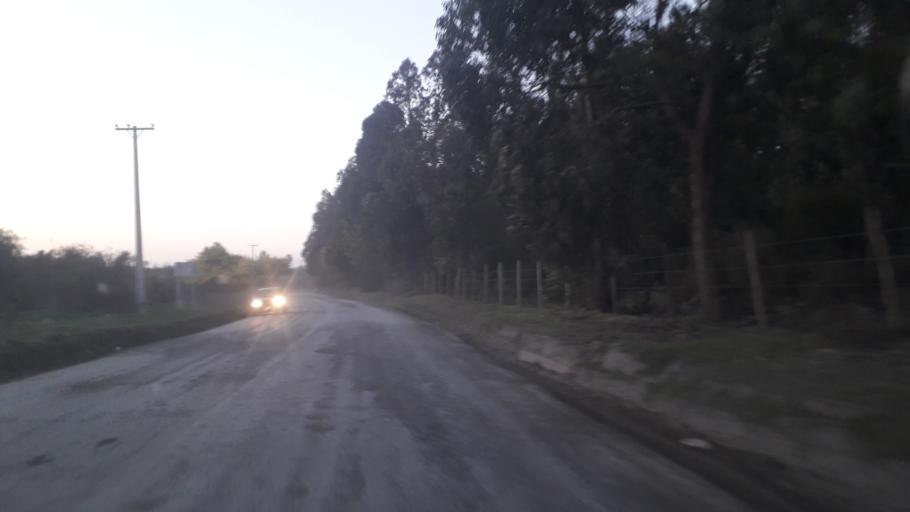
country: CL
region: Valparaiso
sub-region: Provincia de Quillota
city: Hacienda La Calera
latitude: -32.7428
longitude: -71.4178
